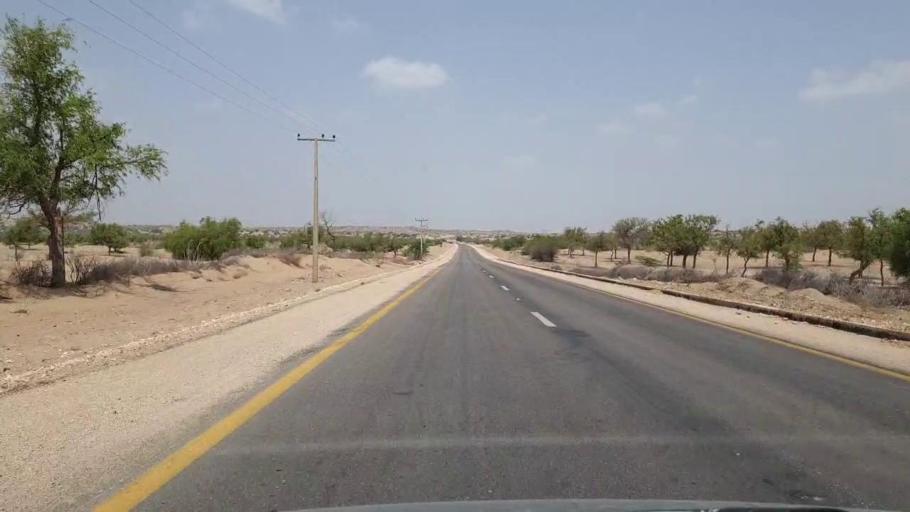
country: PK
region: Sindh
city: Mithi
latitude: 24.8039
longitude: 69.7293
